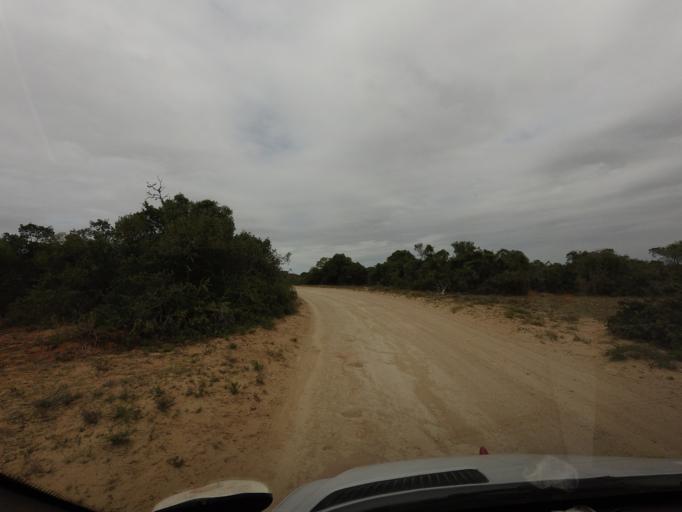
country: ZA
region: Eastern Cape
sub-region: Cacadu District Municipality
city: Kirkwood
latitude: -33.4871
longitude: 25.7667
